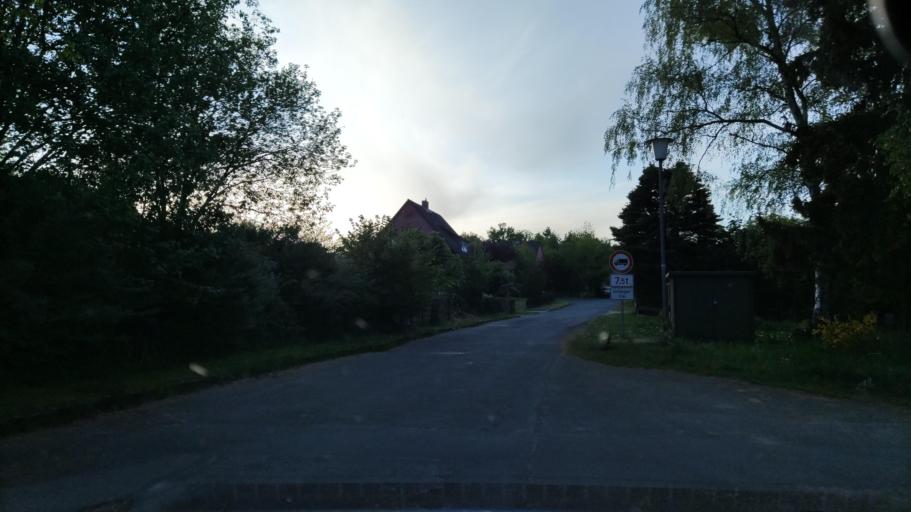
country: DE
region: Lower Saxony
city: Egestorf
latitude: 53.1802
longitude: 10.0664
